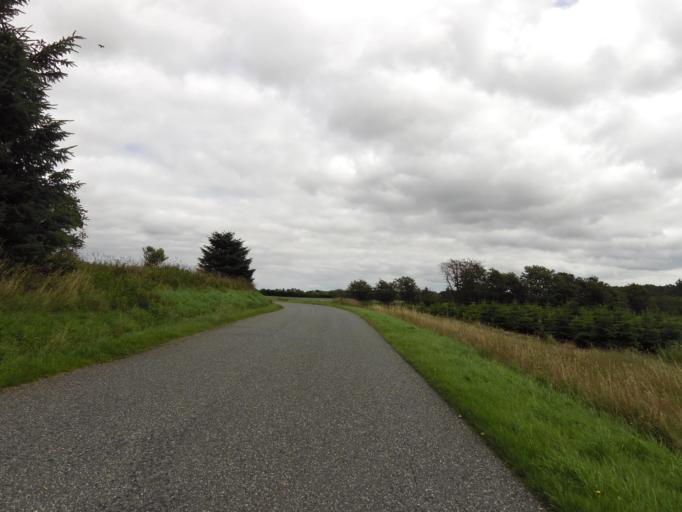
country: DK
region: South Denmark
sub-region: Haderslev Kommune
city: Gram
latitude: 55.2976
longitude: 9.1597
